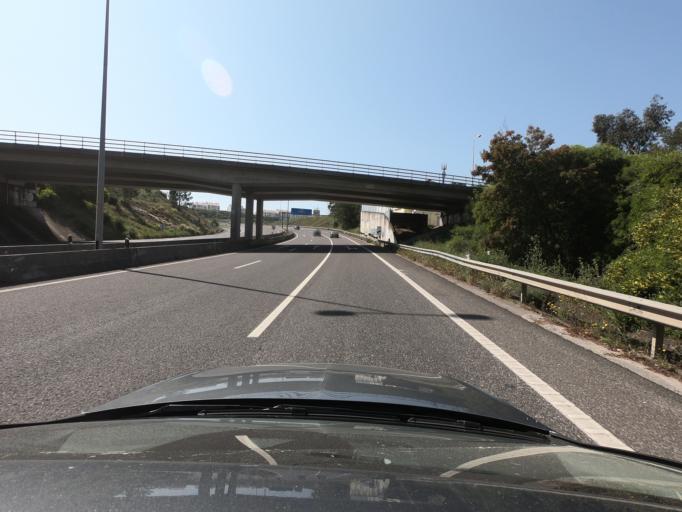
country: PT
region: Lisbon
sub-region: Odivelas
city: Famoes
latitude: 38.7876
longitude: -9.2365
